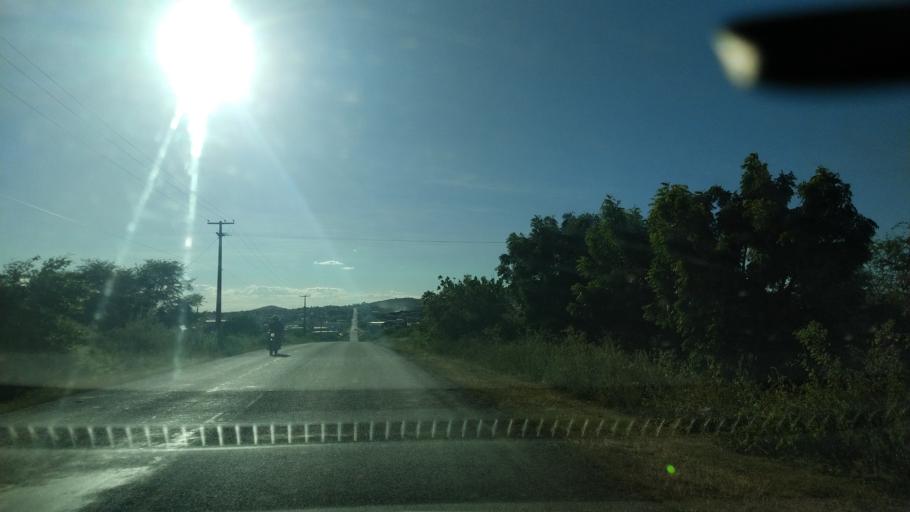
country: BR
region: Rio Grande do Norte
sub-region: Sao Jose Do Campestre
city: Sao Jose do Campestre
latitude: -6.3241
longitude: -35.7009
